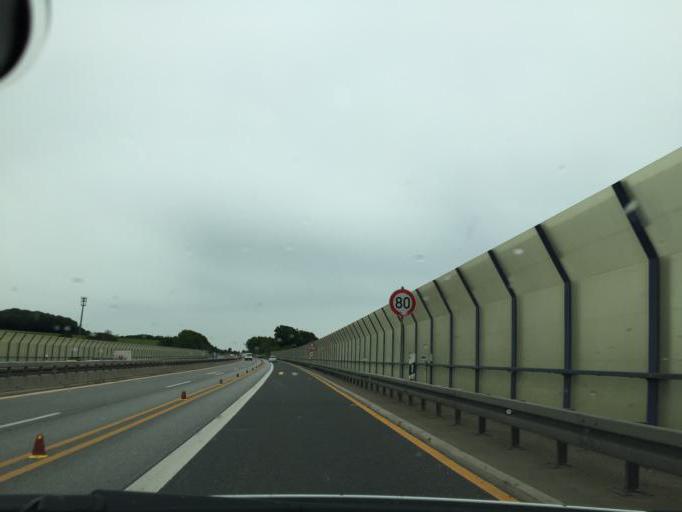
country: DE
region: Bavaria
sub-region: Regierungsbezirk Unterfranken
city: Gadheim
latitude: 50.0082
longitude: 10.3609
